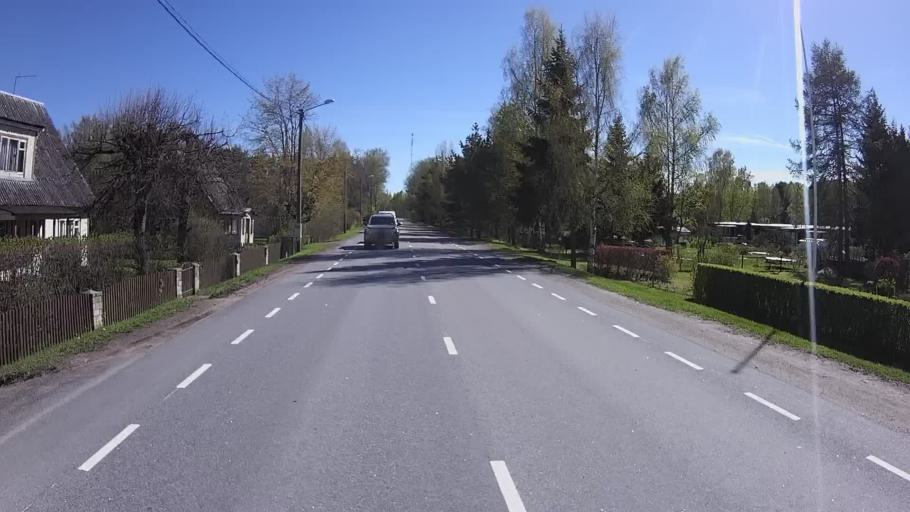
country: EE
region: Harju
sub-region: Loksa linn
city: Loksa
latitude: 59.5736
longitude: 25.7249
